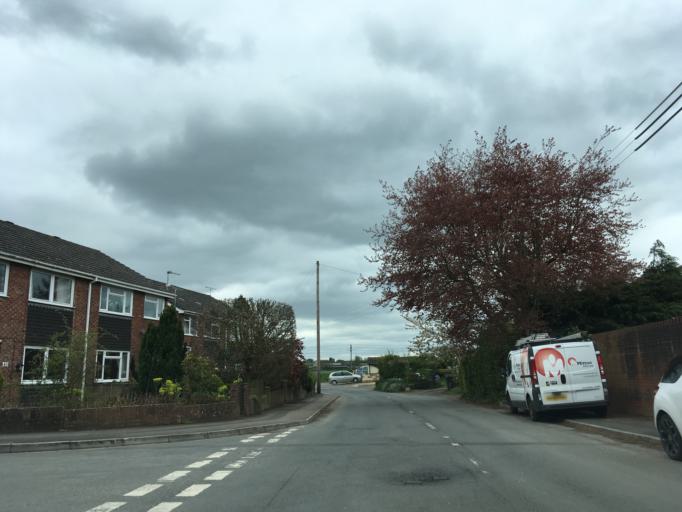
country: GB
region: England
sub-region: Gloucestershire
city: Wotton-under-Edge
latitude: 51.6223
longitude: -2.3680
